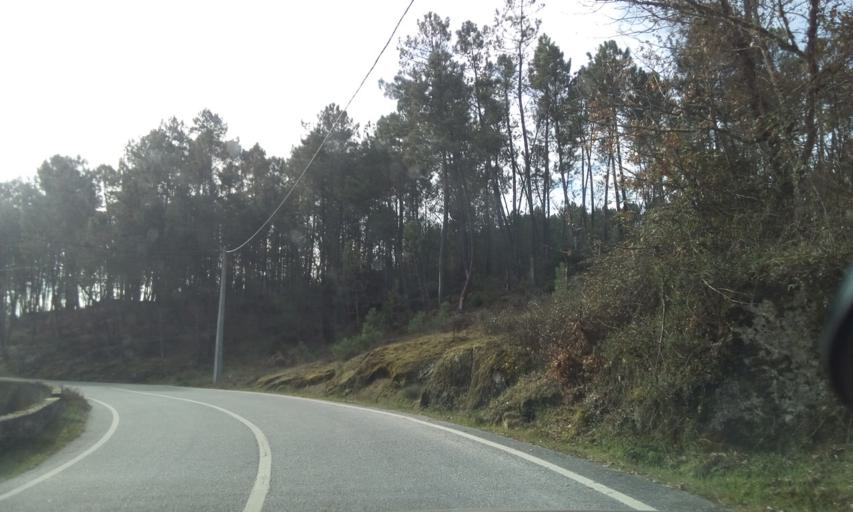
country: PT
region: Guarda
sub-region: Aguiar da Beira
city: Aguiar da Beira
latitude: 40.7248
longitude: -7.5589
